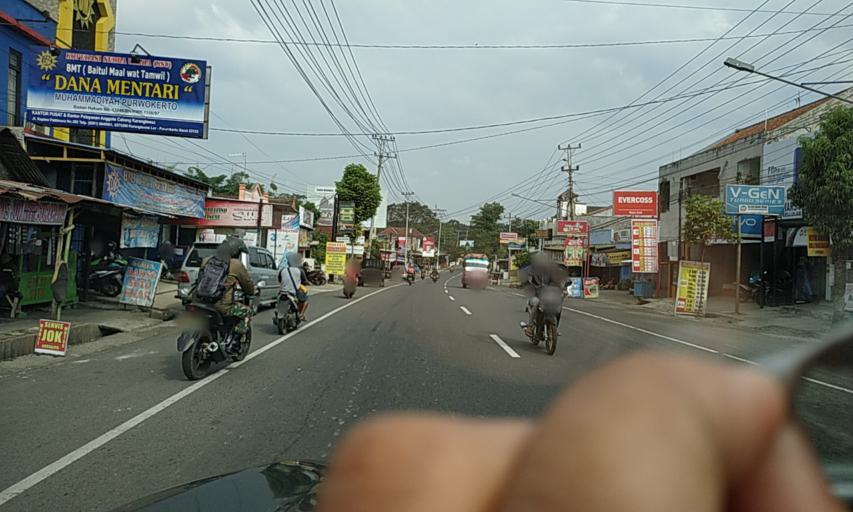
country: ID
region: Central Java
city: Purwokerto
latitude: -7.4202
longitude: 109.1983
